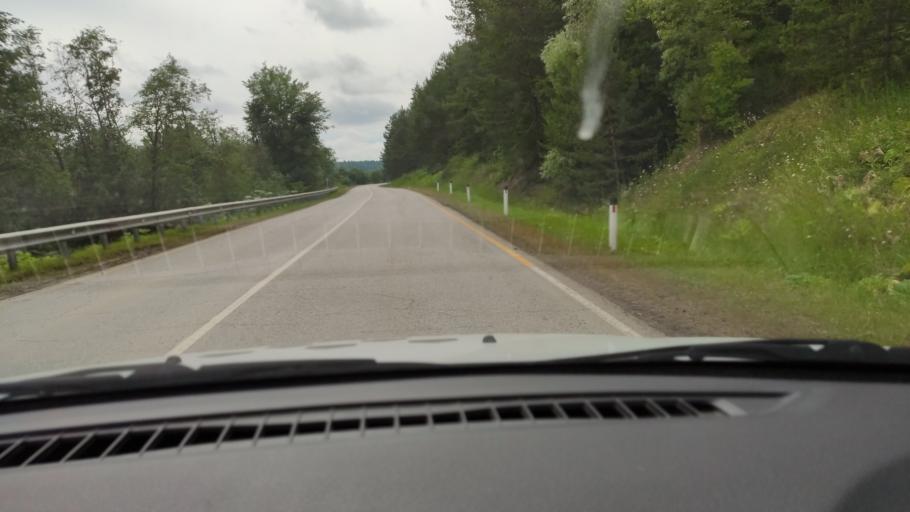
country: RU
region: Perm
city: Kukushtan
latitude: 57.4941
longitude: 56.6421
